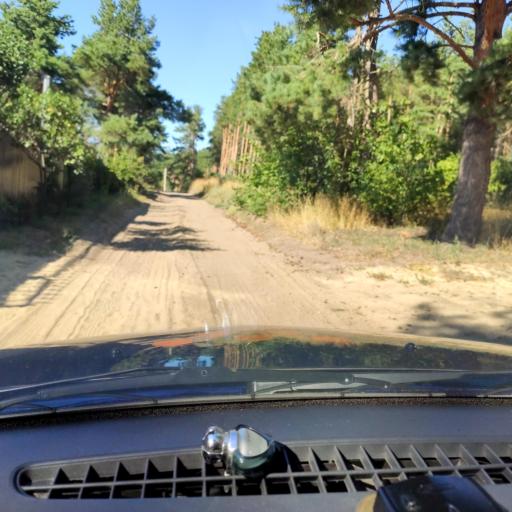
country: RU
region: Voronezj
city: Shilovo
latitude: 51.5363
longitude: 39.1592
